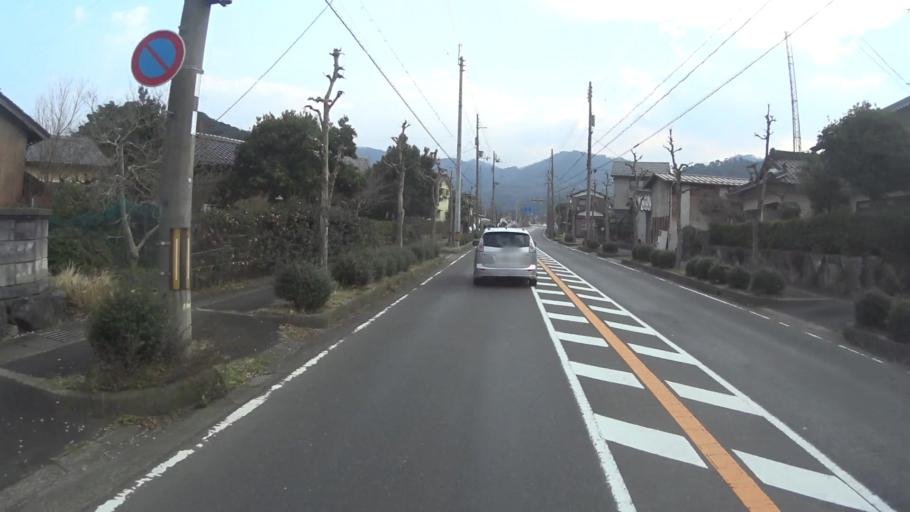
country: JP
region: Kyoto
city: Maizuru
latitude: 35.4556
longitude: 135.3970
